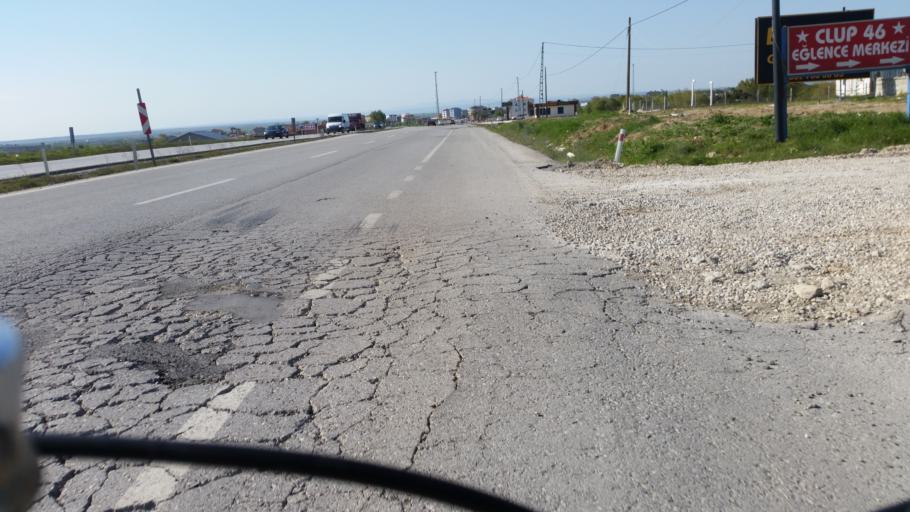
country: TR
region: Tekirdag
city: Cerkezkoey
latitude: 41.3485
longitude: 27.9593
